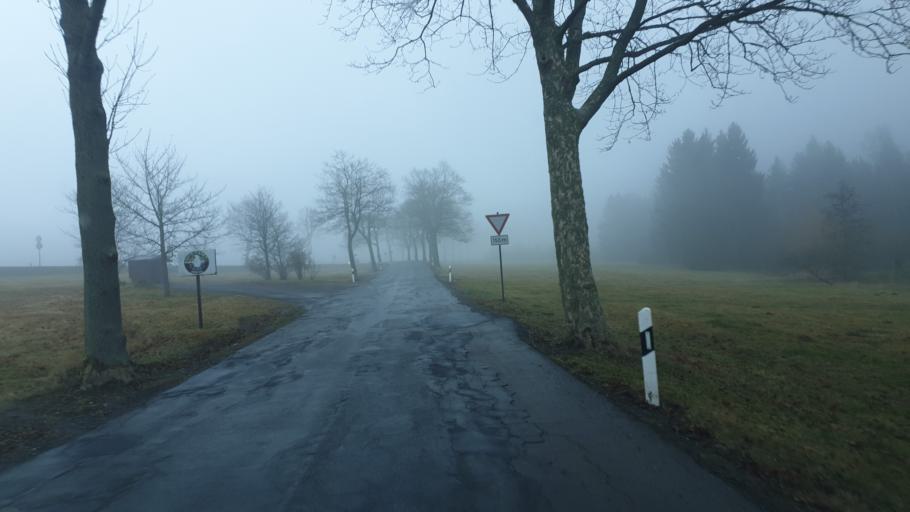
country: DE
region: Saxony
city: Pfaffroda
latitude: 50.7363
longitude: 13.3706
